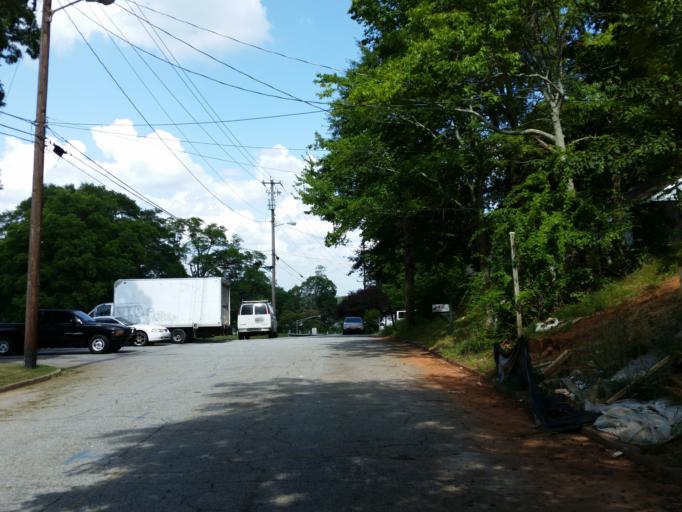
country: US
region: Georgia
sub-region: Cobb County
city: Marietta
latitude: 33.9435
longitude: -84.5432
